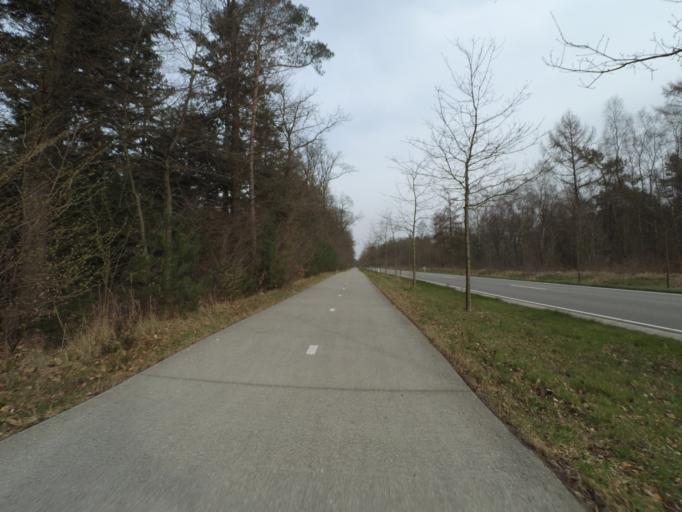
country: NL
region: Gelderland
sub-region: Gemeente Arnhem
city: Hoogkamp
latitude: 52.0324
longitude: 5.8545
